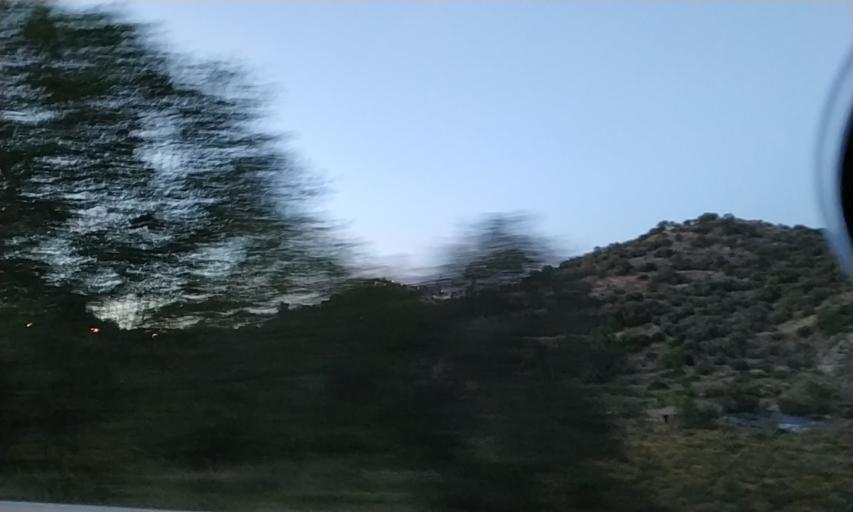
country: ES
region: Extremadura
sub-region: Provincia de Caceres
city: Piedras Albas
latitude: 39.8185
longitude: -6.9826
